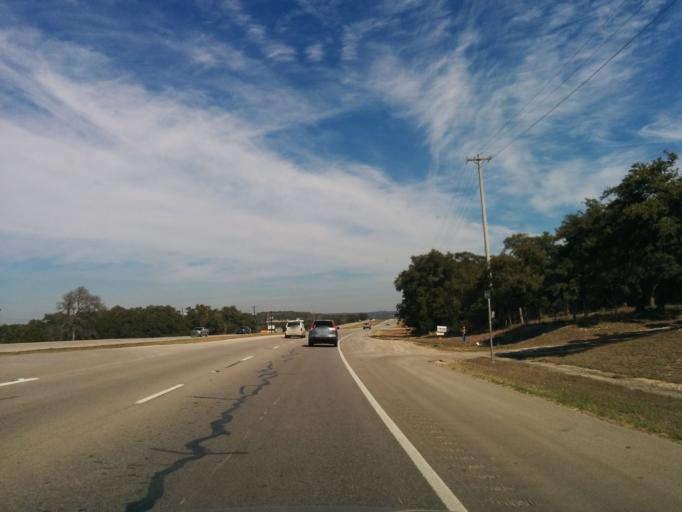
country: US
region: Texas
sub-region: Comal County
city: Bulverde
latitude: 29.8174
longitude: -98.4184
